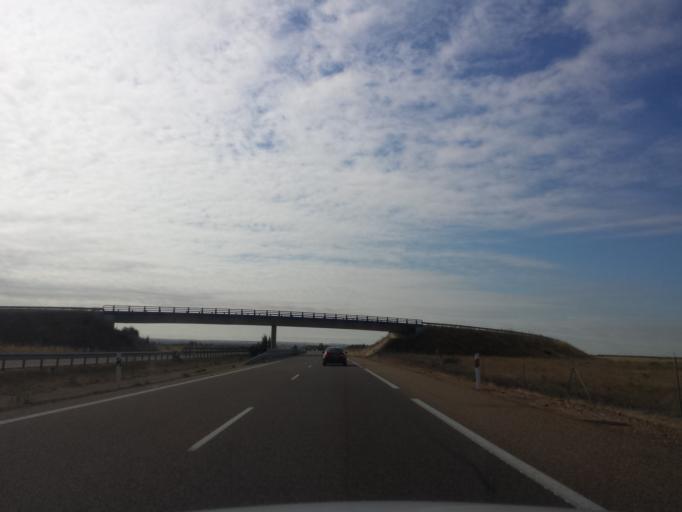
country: ES
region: Castille and Leon
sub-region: Provincia de Leon
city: Onzonilla
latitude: 42.4777
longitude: -5.5939
